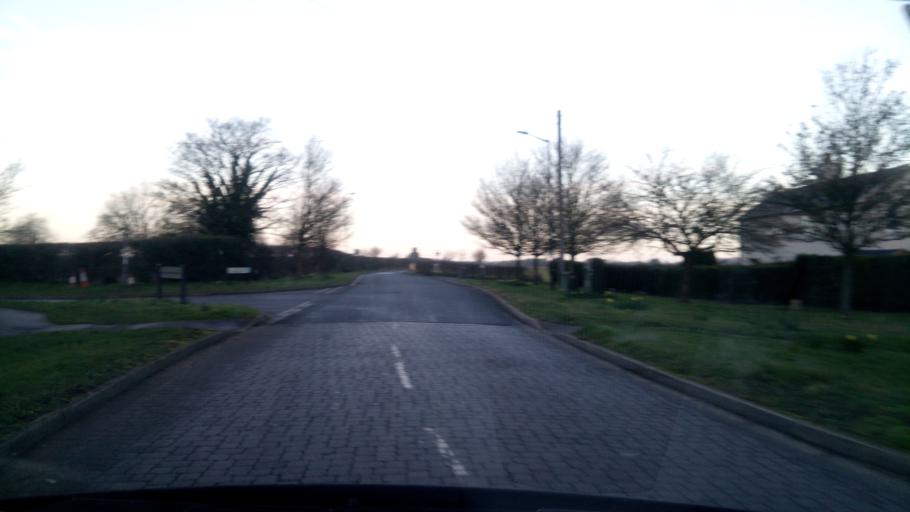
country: GB
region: England
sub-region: Peterborough
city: Castor
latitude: 52.5757
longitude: -0.3535
